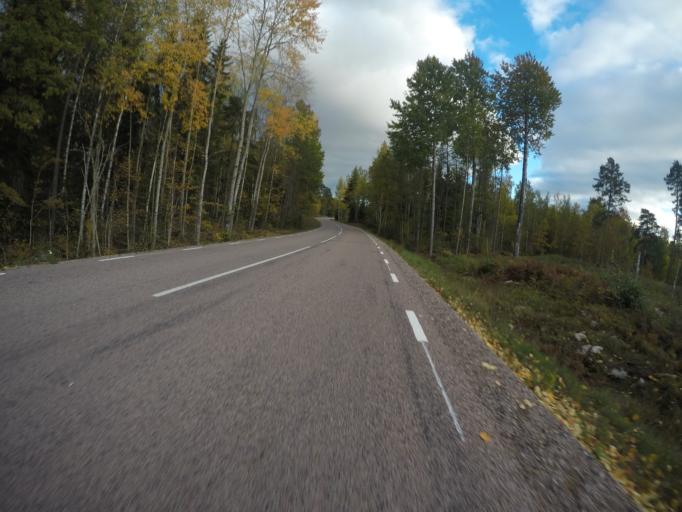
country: SE
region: Vaestmanland
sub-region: Arboga Kommun
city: Tyringe
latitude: 59.3079
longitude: 15.9970
